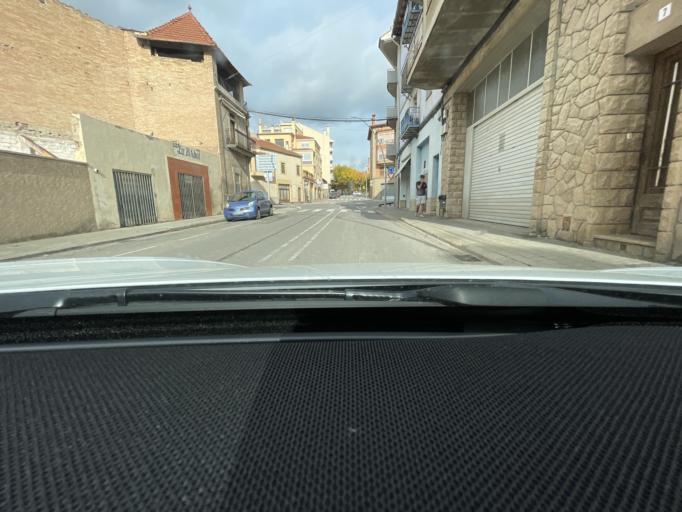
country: ES
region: Catalonia
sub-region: Provincia de Lleida
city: Solsona
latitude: 41.9930
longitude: 1.5139
